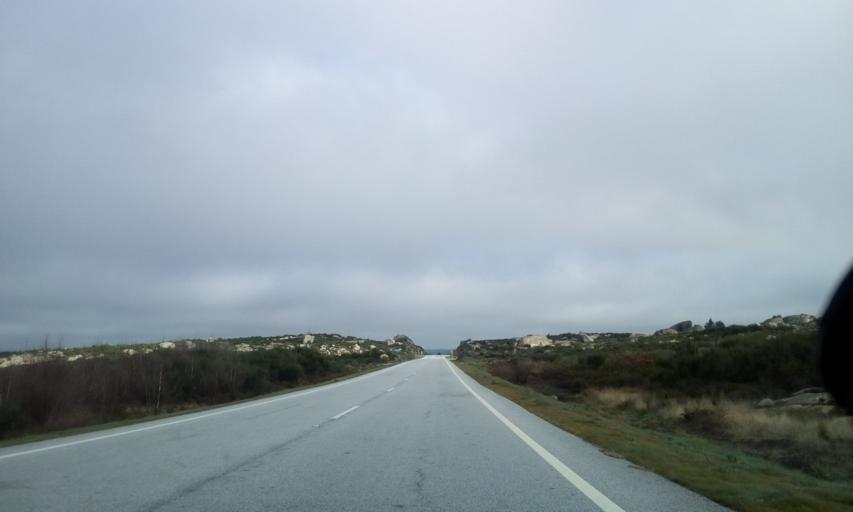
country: PT
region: Guarda
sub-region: Aguiar da Beira
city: Aguiar da Beira
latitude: 40.7641
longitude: -7.5022
